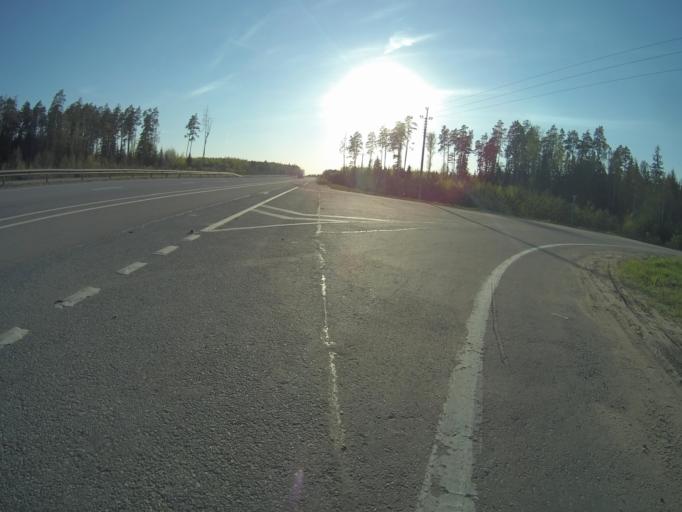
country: RU
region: Vladimir
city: Orgtrud
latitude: 56.1039
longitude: 40.6546
